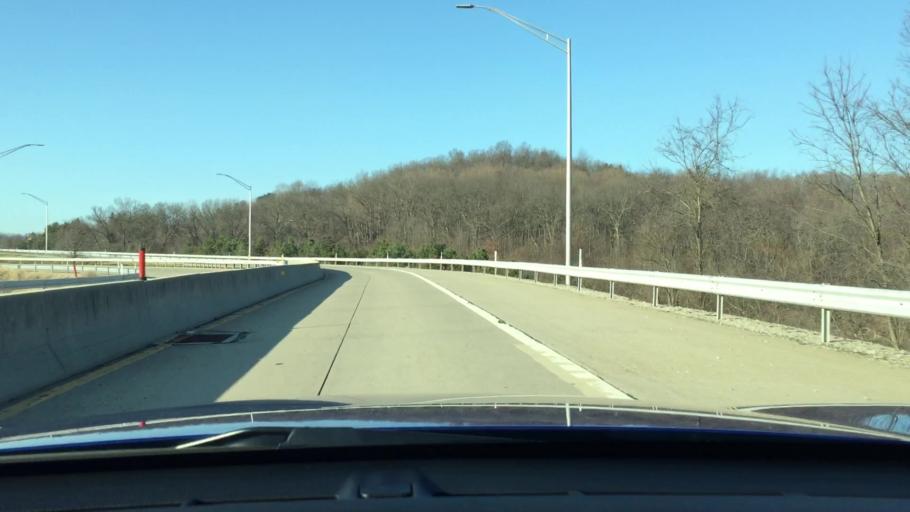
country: US
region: Pennsylvania
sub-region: Westmoreland County
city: New Stanton
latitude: 40.2345
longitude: -79.5998
